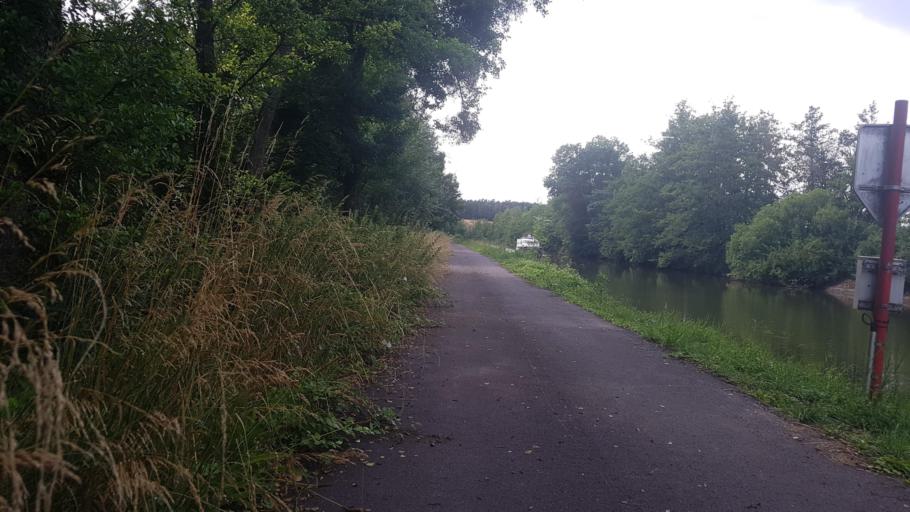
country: FR
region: Lorraine
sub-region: Departement de la Moselle
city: Dieuze
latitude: 48.6961
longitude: 6.7442
